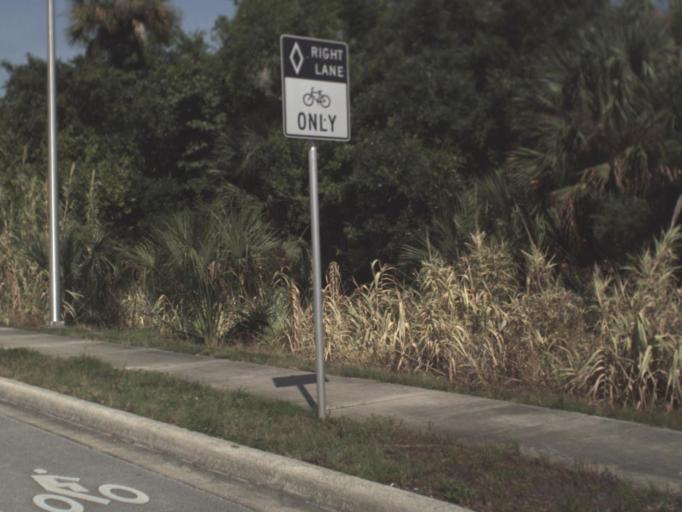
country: US
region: Florida
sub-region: Duval County
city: Atlantic Beach
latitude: 30.3701
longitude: -81.4125
